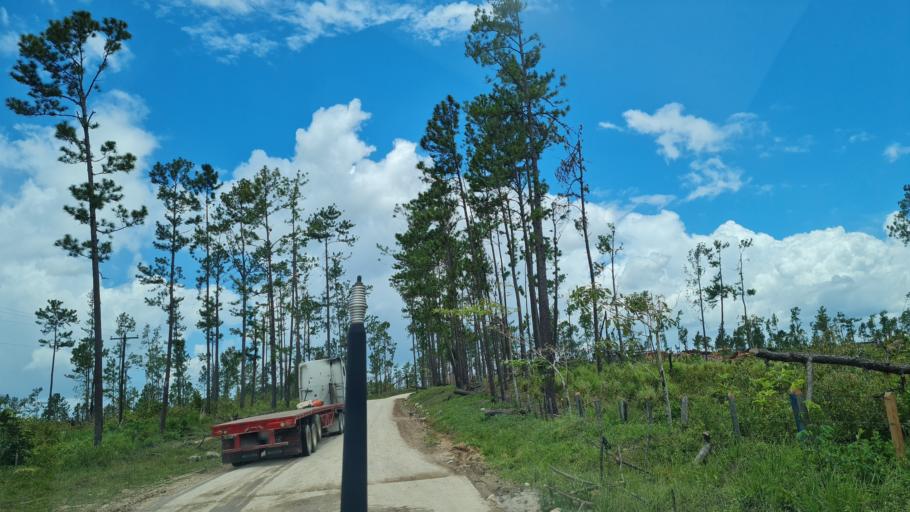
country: NI
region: Atlantico Sur
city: La Cruz de Rio Grande
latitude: 13.5692
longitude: -84.3177
